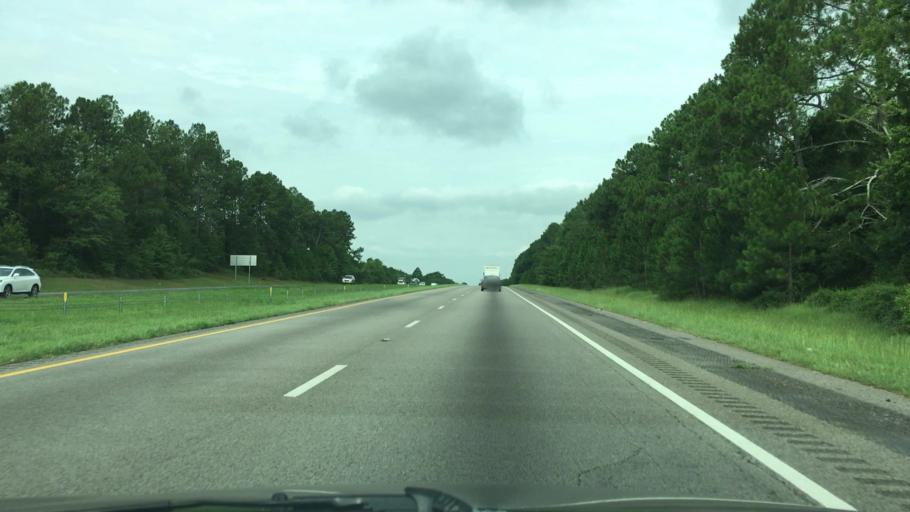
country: US
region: South Carolina
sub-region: Aiken County
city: Graniteville
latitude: 33.6355
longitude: -81.7636
